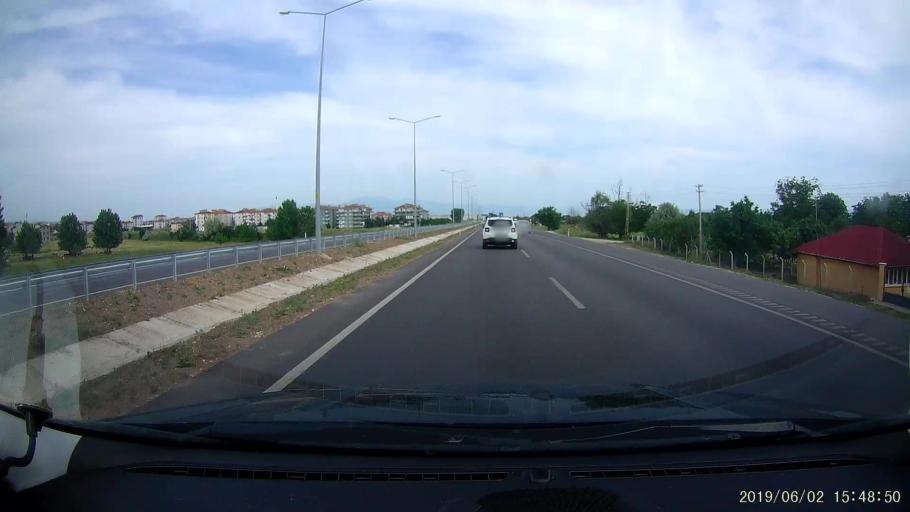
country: TR
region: Amasya
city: Merzifon
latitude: 40.8603
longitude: 35.4496
